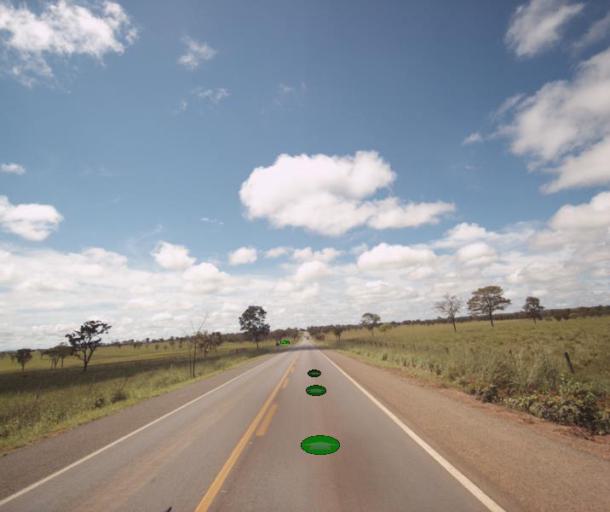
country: BR
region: Goias
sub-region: Padre Bernardo
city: Padre Bernardo
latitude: -15.1597
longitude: -48.3133
